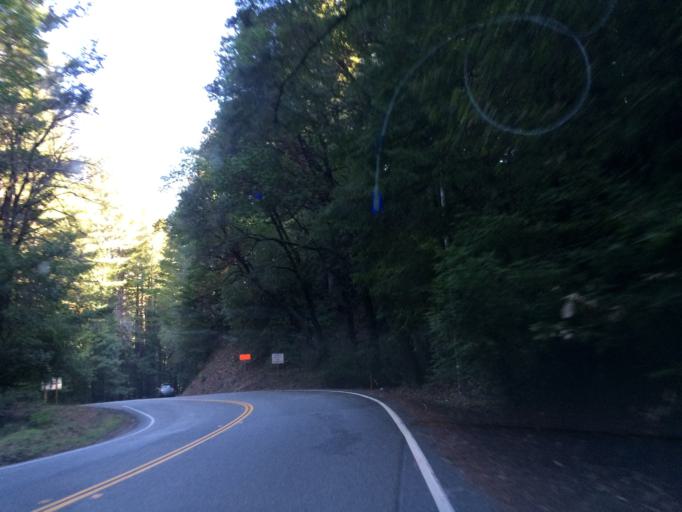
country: US
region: California
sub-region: Santa Cruz County
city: Boulder Creek
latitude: 37.2042
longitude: -122.1449
